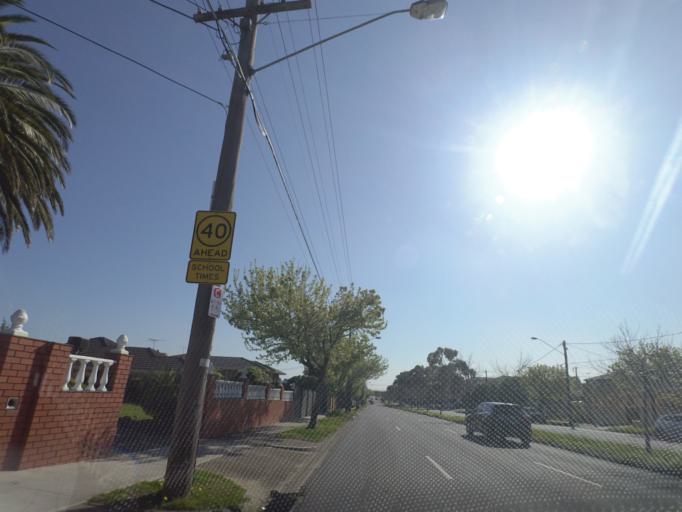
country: AU
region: Victoria
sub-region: Manningham
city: Templestowe Lower
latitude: -37.7731
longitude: 145.1085
